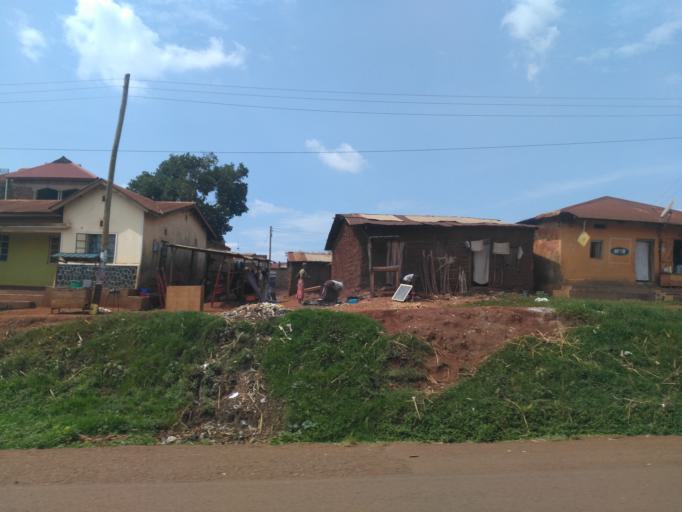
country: UG
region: Eastern Region
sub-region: Jinja District
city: Bugembe
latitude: 0.4644
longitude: 33.2331
